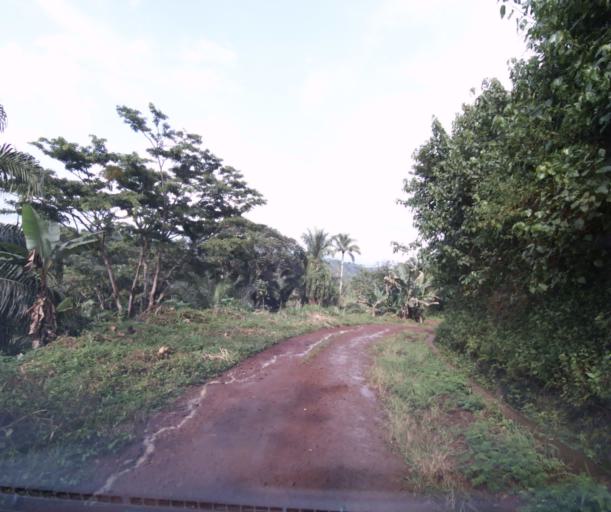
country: CM
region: Littoral
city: Melong
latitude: 5.0606
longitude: 9.9752
